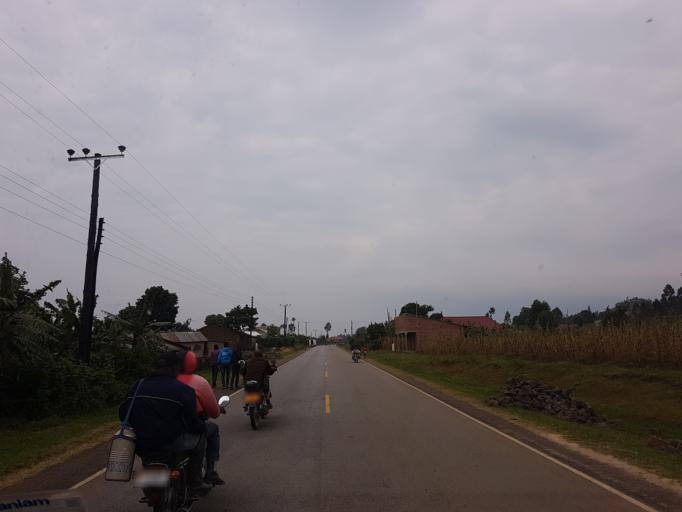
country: UG
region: Western Region
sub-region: Kisoro District
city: Kisoro
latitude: -1.3019
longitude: 29.7230
